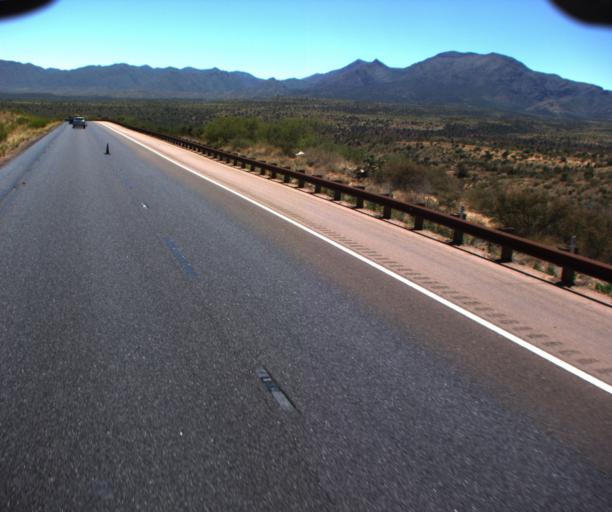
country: US
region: Arizona
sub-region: Gila County
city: Payson
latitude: 34.1306
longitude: -111.3553
